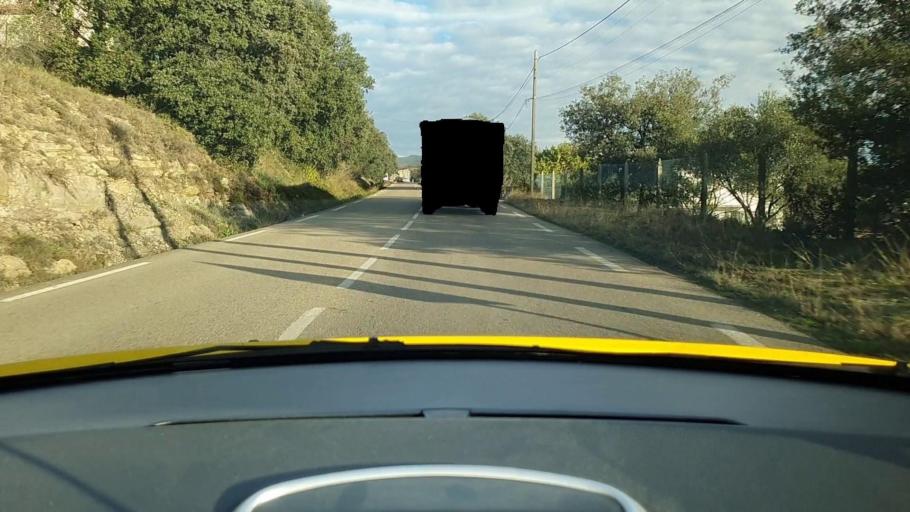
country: FR
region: Languedoc-Roussillon
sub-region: Departement du Gard
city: Saint-Martin-de-Valgalgues
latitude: 44.1697
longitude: 4.0835
